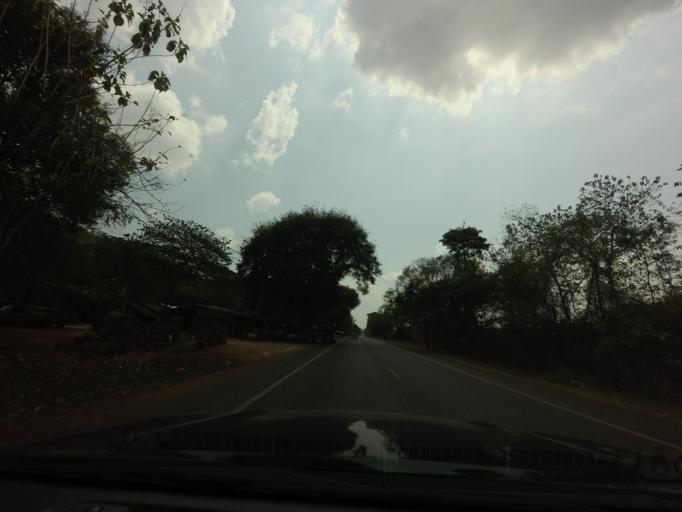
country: TH
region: Kanchanaburi
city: Sai Yok
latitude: 14.1497
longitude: 99.1434
